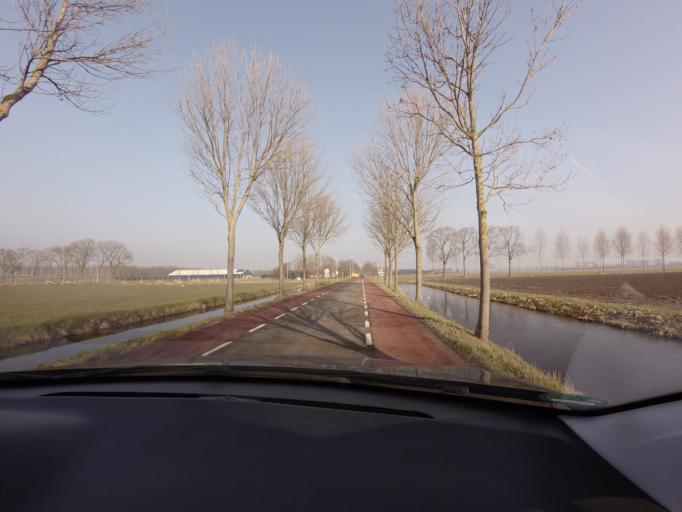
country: NL
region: North Holland
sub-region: Gemeente Beemster
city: Halfweg
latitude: 52.5689
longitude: 4.9750
